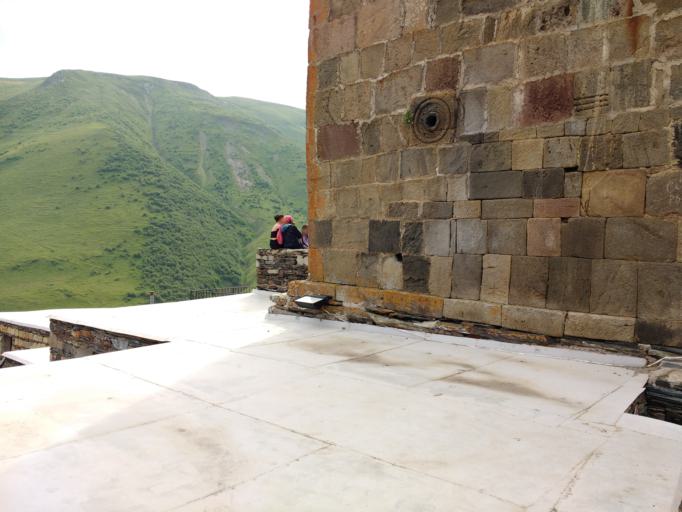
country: GE
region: Mtskheta-Mtianeti
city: Step'antsminda
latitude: 42.6622
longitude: 44.6206
